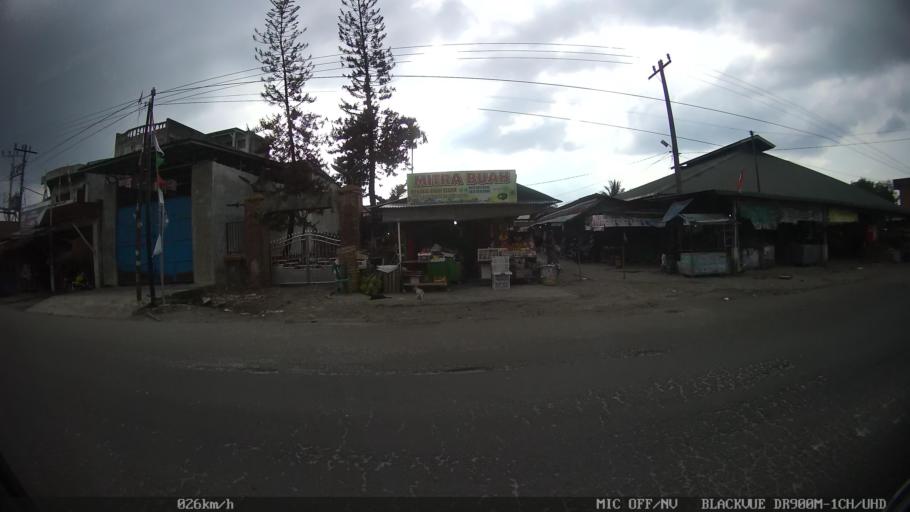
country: ID
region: North Sumatra
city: Sunggal
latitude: 3.5265
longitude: 98.6199
